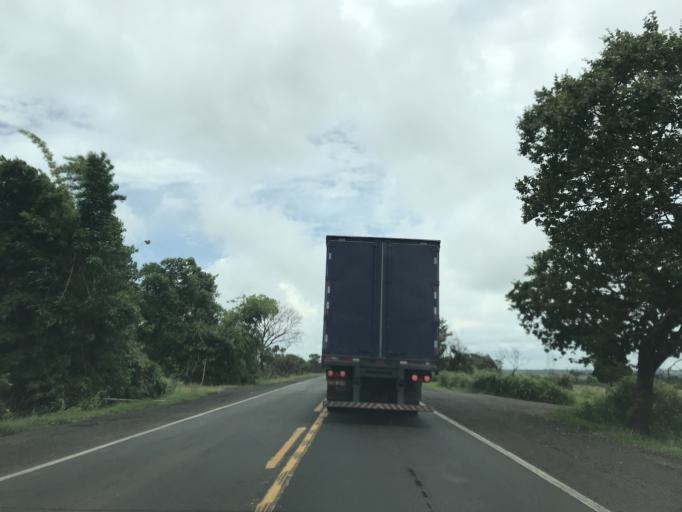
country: BR
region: Minas Gerais
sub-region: Frutal
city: Frutal
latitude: -19.7838
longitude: -48.9659
